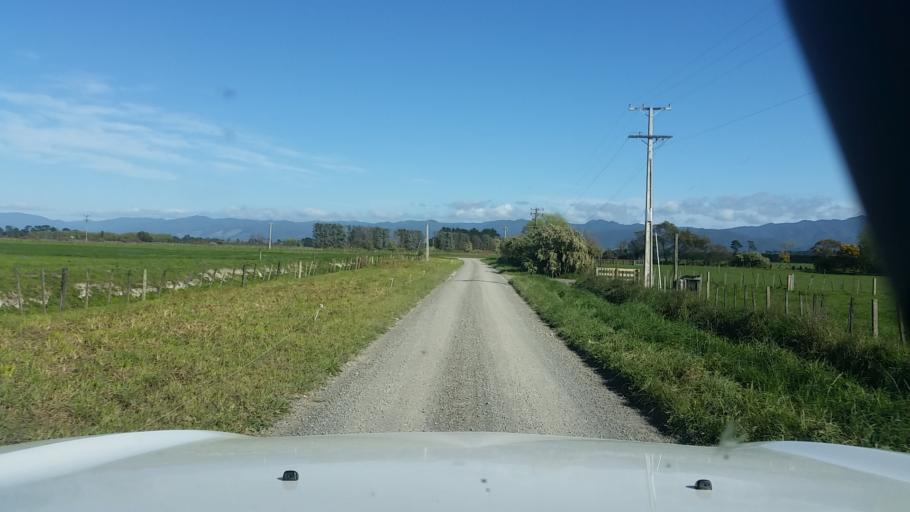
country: NZ
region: Wellington
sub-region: South Wairarapa District
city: Waipawa
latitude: -41.1430
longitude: 175.4072
